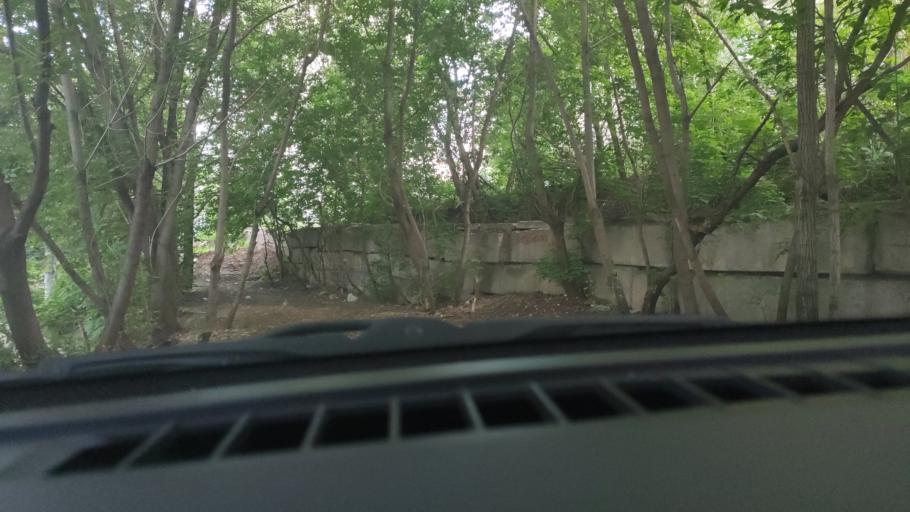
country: RU
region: Perm
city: Perm
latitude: 57.9798
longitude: 56.2777
